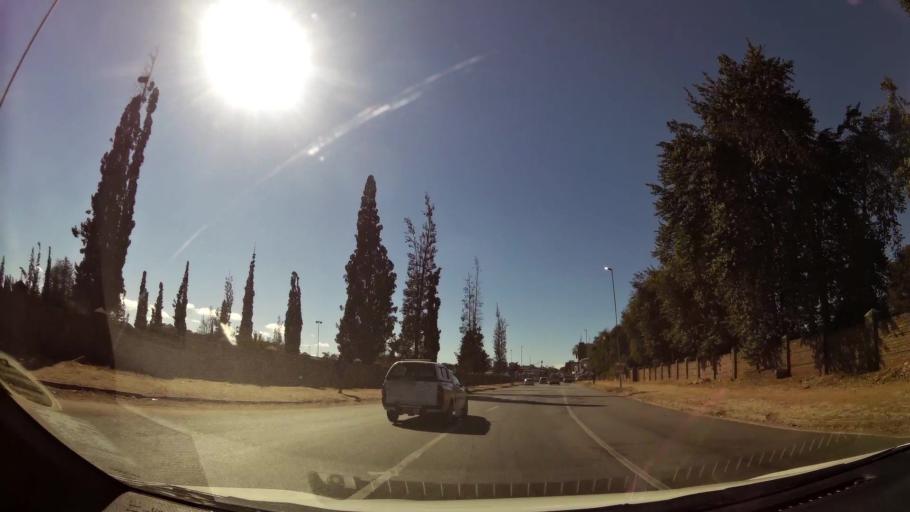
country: ZA
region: Limpopo
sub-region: Capricorn District Municipality
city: Polokwane
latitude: -23.9105
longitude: 29.4457
